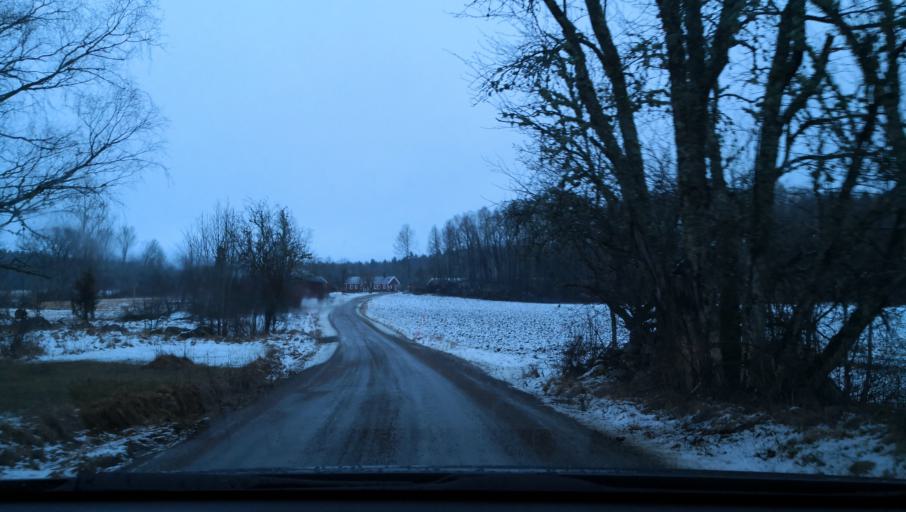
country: SE
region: Vaestmanland
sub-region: Kungsors Kommun
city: Kungsoer
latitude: 59.4036
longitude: 16.2037
